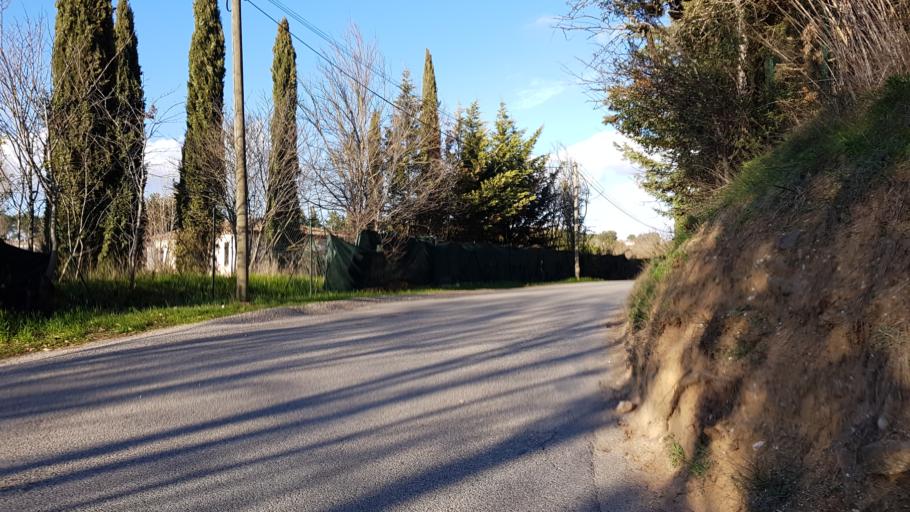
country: FR
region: Provence-Alpes-Cote d'Azur
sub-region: Departement des Bouches-du-Rhone
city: Bouc-Bel-Air
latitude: 43.4906
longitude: 5.3897
